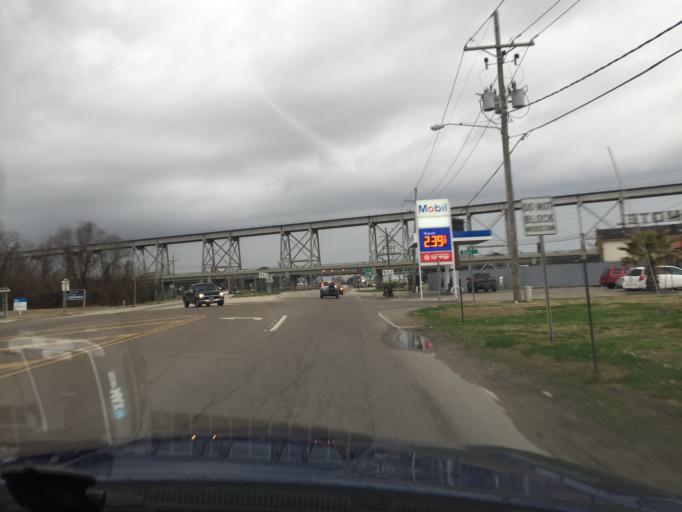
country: US
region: Louisiana
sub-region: Jefferson Parish
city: Bridge City
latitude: 29.9301
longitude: -90.1629
